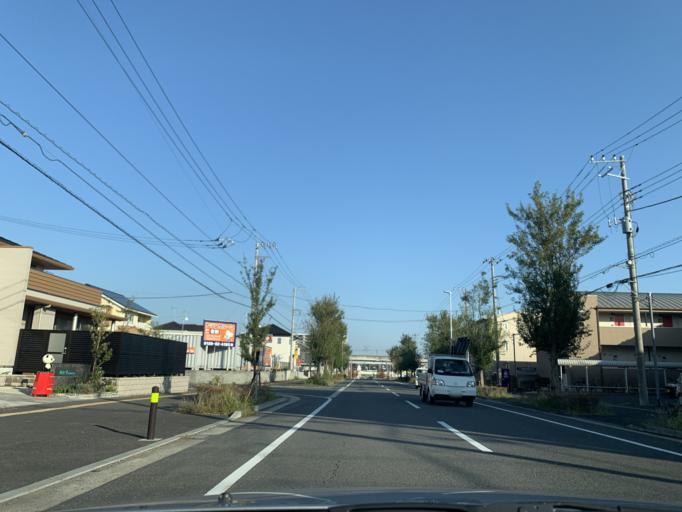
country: JP
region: Ibaraki
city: Moriya
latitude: 35.9133
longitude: 139.9542
